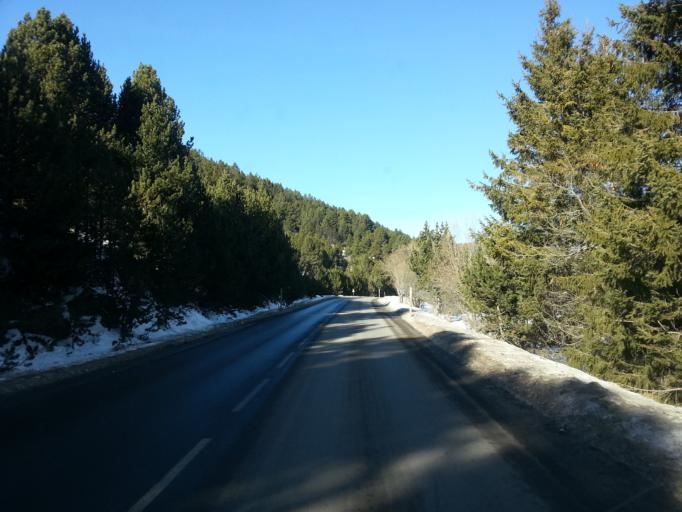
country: ES
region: Catalonia
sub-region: Provincia de Girona
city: Llivia
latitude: 42.5643
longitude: 2.0732
